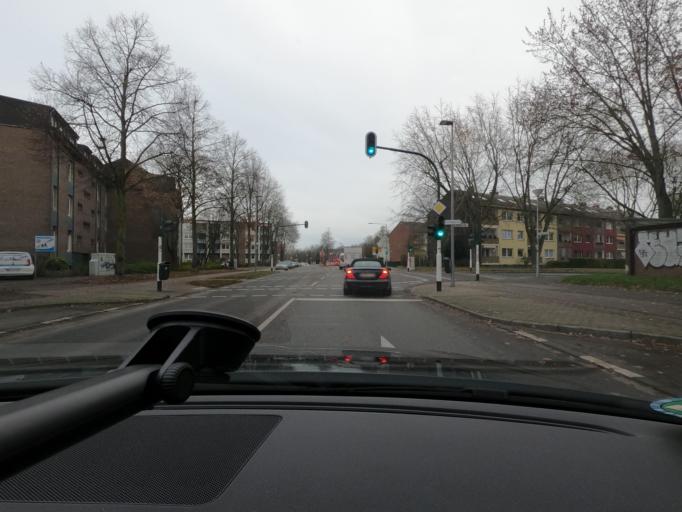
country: DE
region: North Rhine-Westphalia
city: Tonisvorst
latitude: 51.3467
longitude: 6.5235
